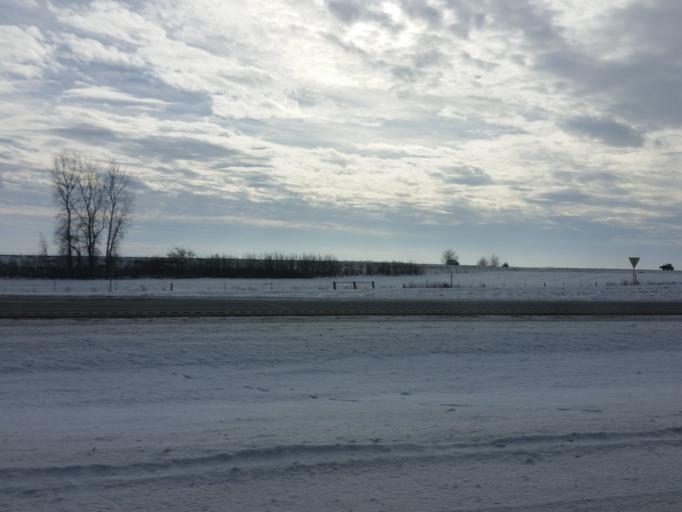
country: US
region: Iowa
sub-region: Buchanan County
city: Independence
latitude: 42.4483
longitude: -91.9161
